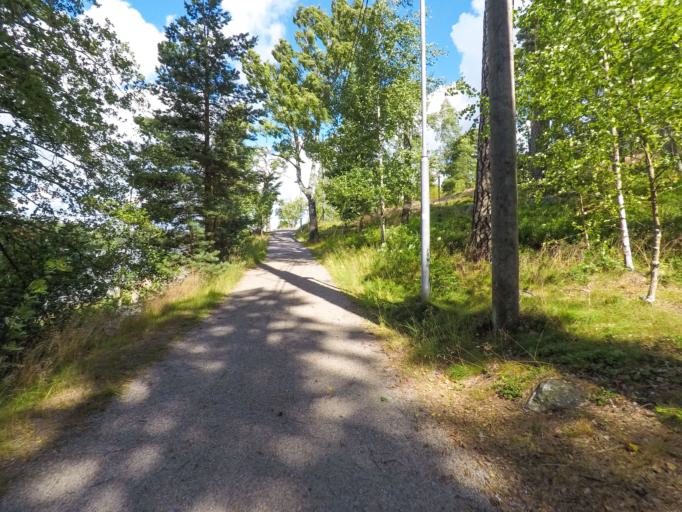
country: FI
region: Uusimaa
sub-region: Helsinki
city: Helsinki
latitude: 60.1777
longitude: 25.0215
